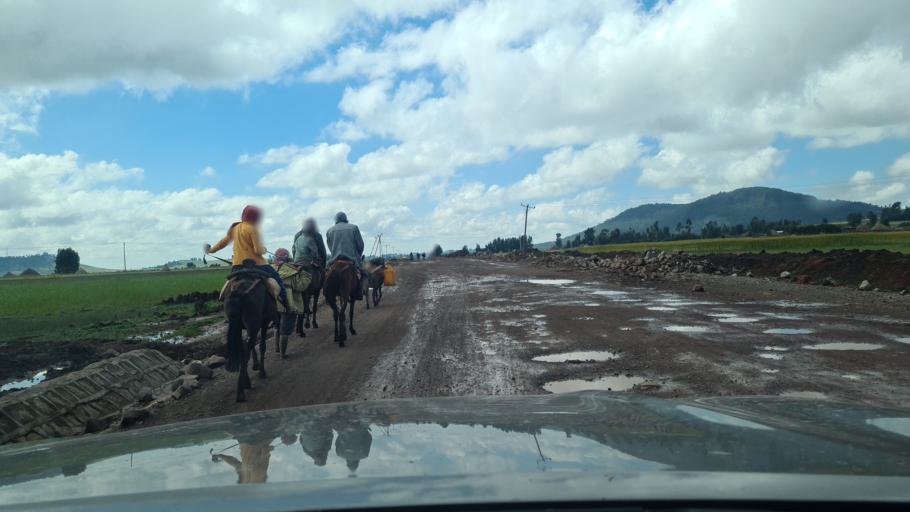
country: ET
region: Oromiya
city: Huruta
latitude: 8.0927
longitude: 39.5367
